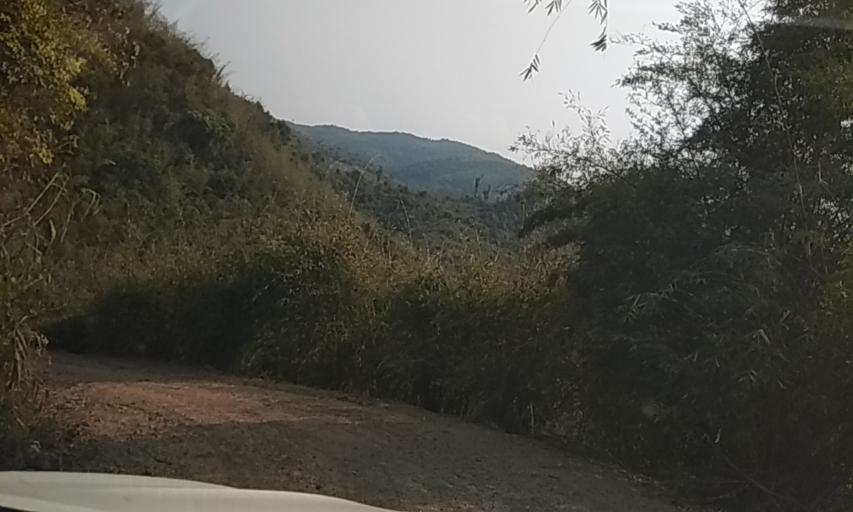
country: LA
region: Louangphabang
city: Louangphabang
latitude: 20.0379
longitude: 101.7968
